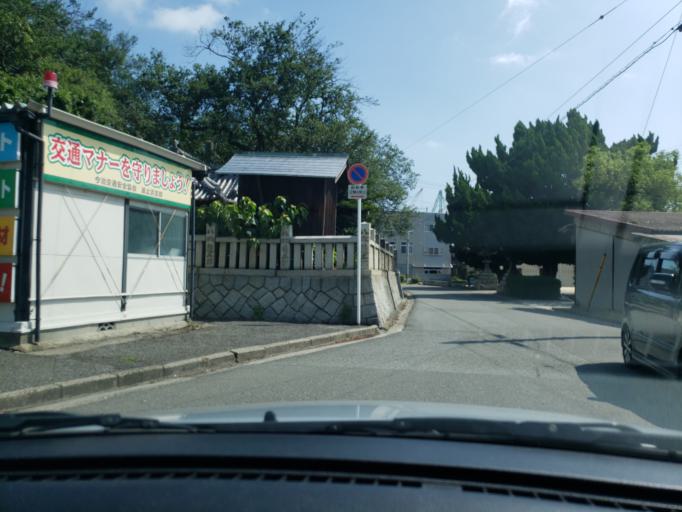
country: JP
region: Ehime
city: Hojo
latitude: 34.1056
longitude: 132.9669
